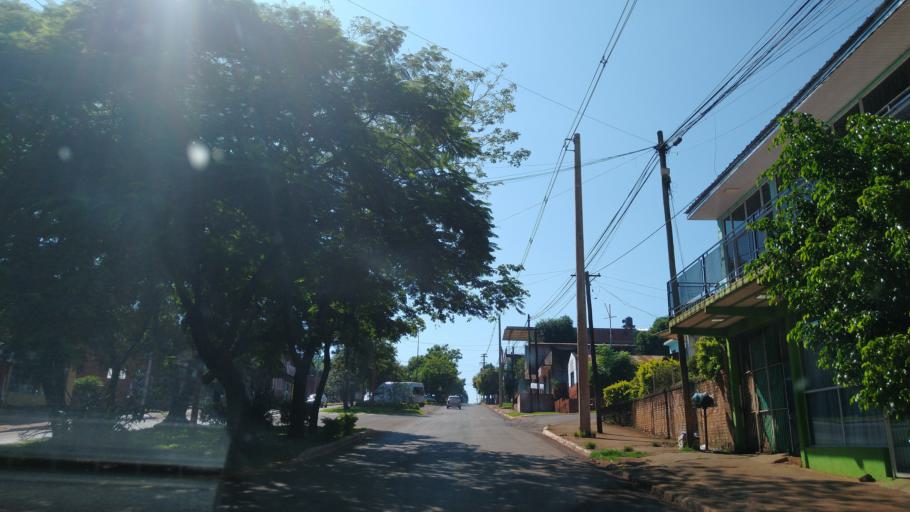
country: AR
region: Misiones
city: Puerto Esperanza
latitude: -26.0226
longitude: -54.6078
